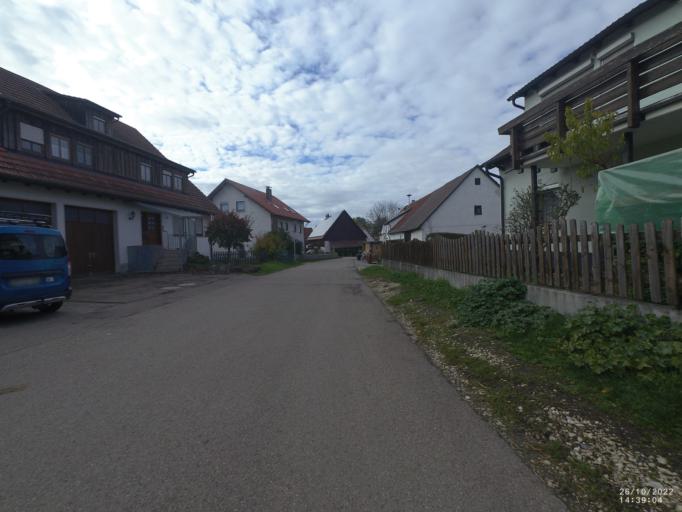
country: DE
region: Baden-Wuerttemberg
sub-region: Regierungsbezirk Stuttgart
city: Donzdorf
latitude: 48.6594
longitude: 9.8188
